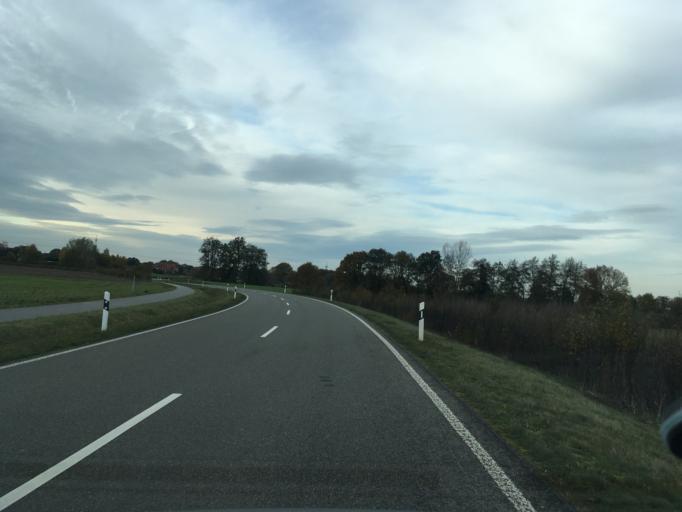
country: DE
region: North Rhine-Westphalia
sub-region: Regierungsbezirk Munster
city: Velen
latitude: 51.8955
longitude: 6.9275
